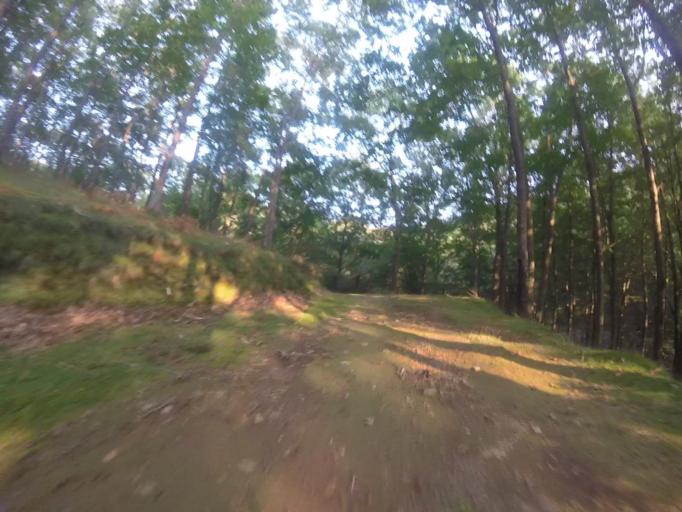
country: ES
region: Navarre
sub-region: Provincia de Navarra
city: Arano
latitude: 43.2518
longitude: -1.8295
